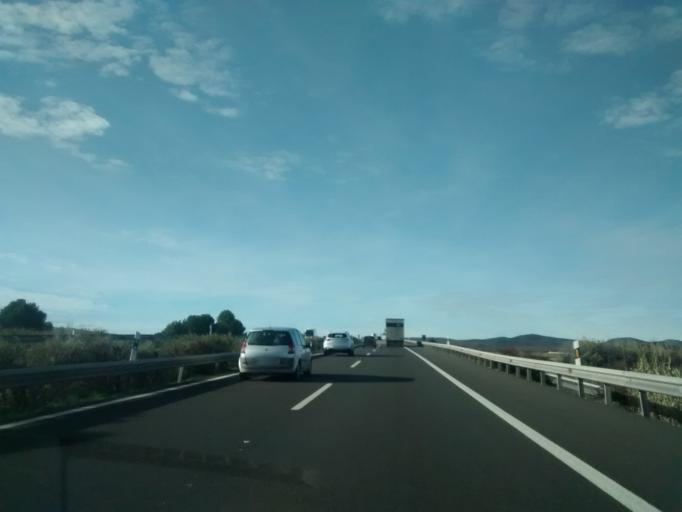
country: ES
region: Aragon
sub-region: Provincia de Zaragoza
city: La Almunia de Dona Godina
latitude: 41.4856
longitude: -1.3800
